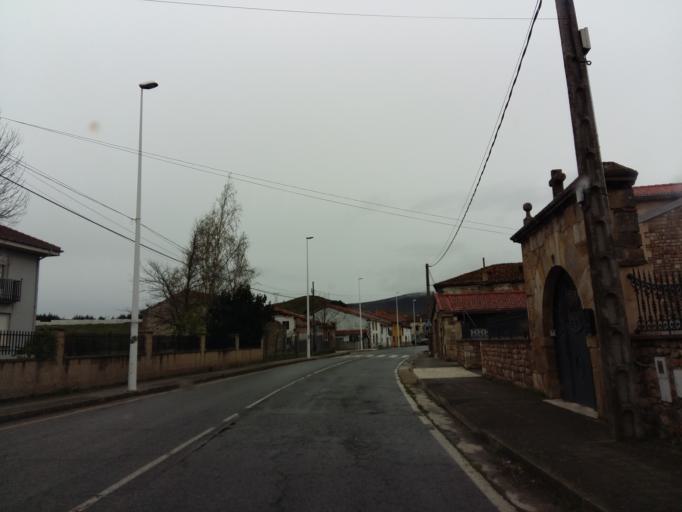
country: ES
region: Cantabria
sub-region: Provincia de Cantabria
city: Reinosa
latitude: 42.9799
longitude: -4.1494
